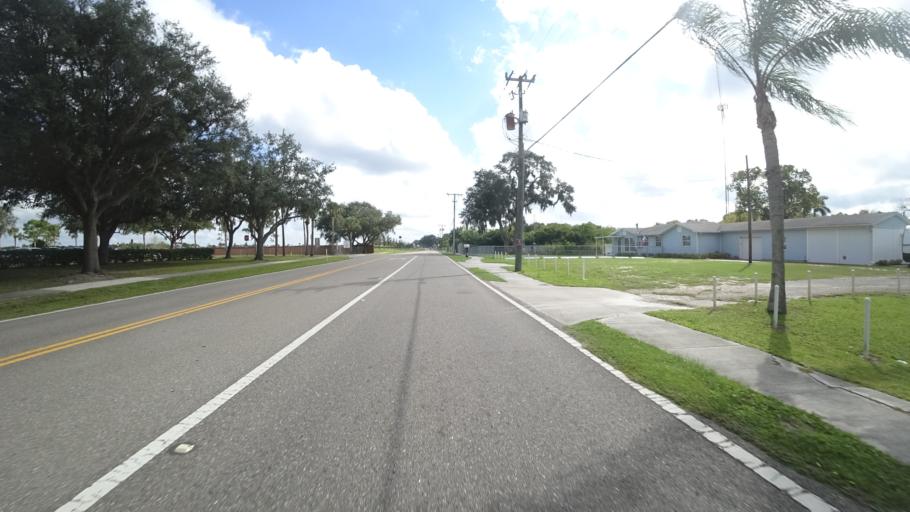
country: US
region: Florida
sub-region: Manatee County
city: Samoset
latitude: 27.4769
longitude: -82.5372
